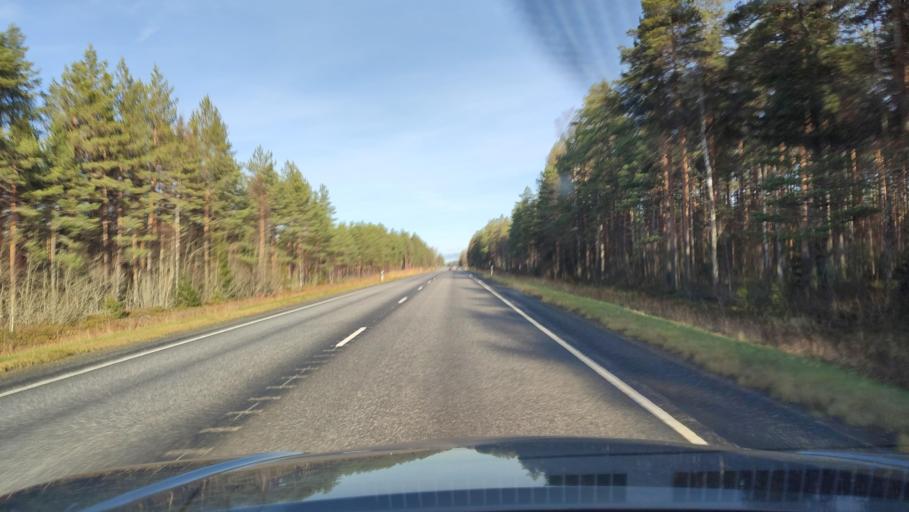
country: FI
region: Ostrobothnia
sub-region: Vaasa
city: Malax
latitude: 62.7967
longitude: 21.6741
